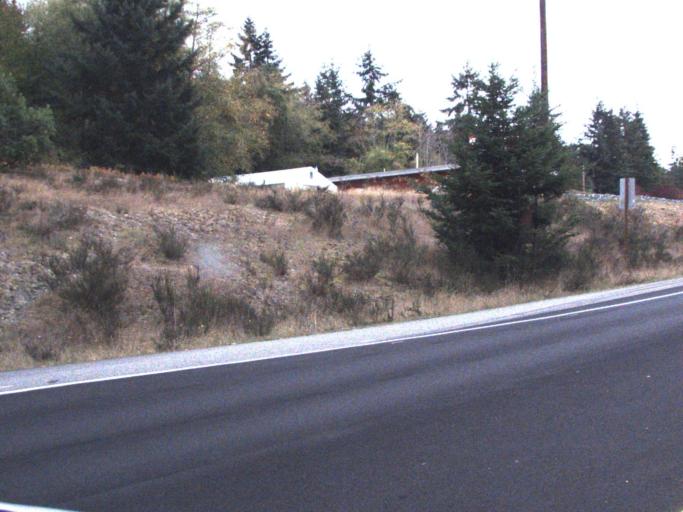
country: US
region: Washington
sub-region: Island County
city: Freeland
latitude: 48.0035
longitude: -122.4611
